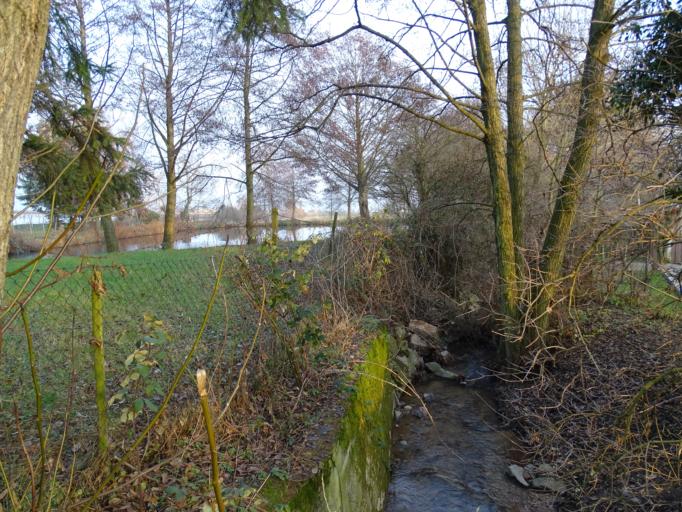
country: DE
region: Rheinland-Pfalz
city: Oestrich-Winkel
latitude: 49.9965
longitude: 7.9880
